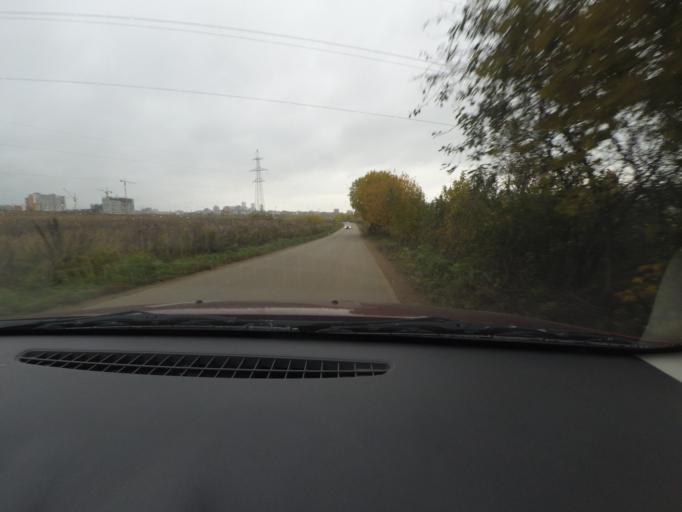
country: RU
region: Nizjnij Novgorod
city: Afonino
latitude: 56.2721
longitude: 44.0577
